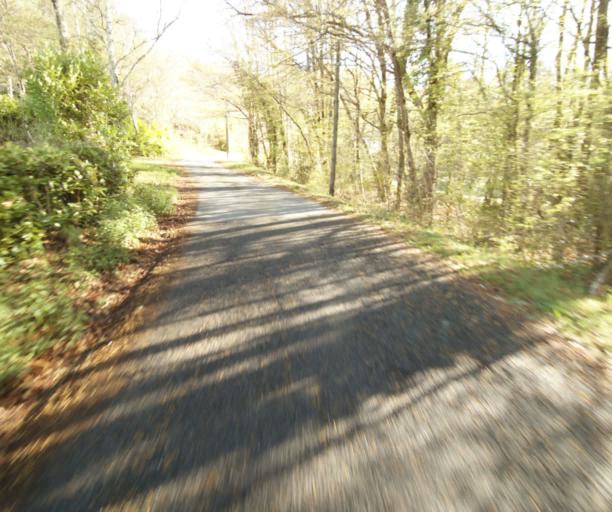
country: FR
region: Limousin
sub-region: Departement de la Correze
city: Laguenne
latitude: 45.2583
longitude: 1.8545
